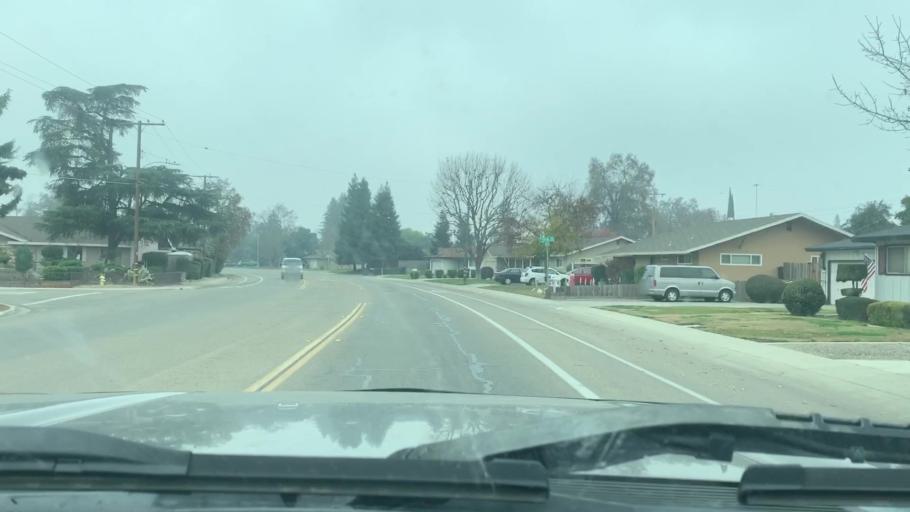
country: US
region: California
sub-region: Tulare County
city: Visalia
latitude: 36.3195
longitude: -119.3273
